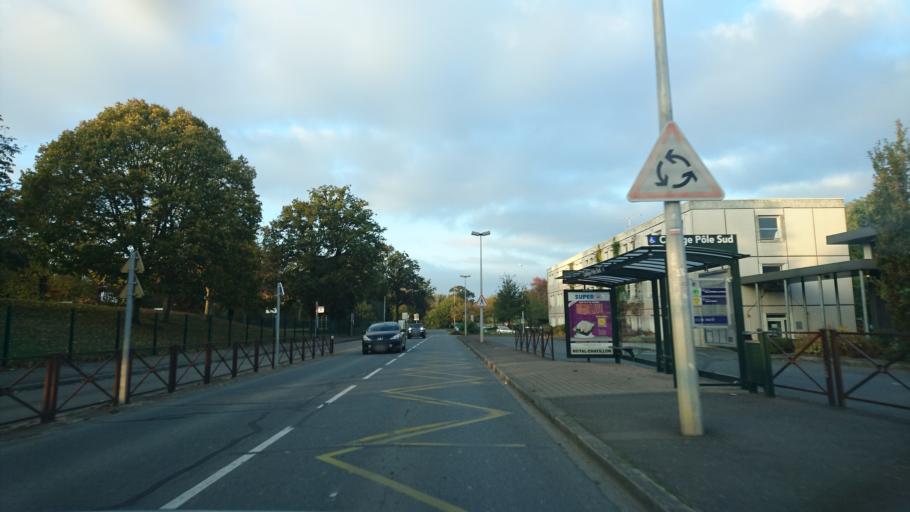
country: FR
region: Brittany
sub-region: Departement d'Ille-et-Vilaine
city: Chartres-de-Bretagne
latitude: 48.0415
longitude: -1.6961
